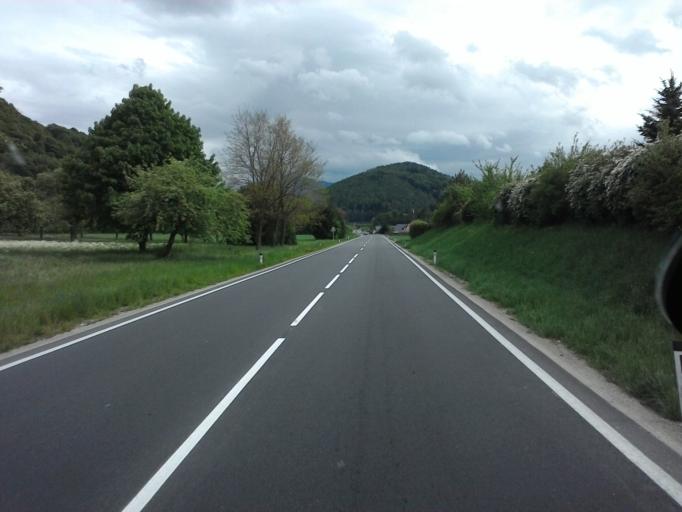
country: AT
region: Upper Austria
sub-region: Politischer Bezirk Kirchdorf an der Krems
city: Micheldorf in Oberoesterreich
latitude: 47.8749
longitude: 14.1304
